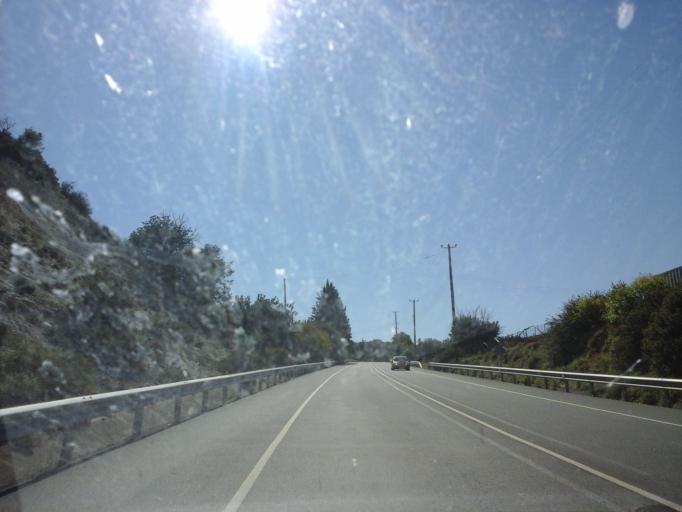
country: CY
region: Limassol
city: Pano Polemidia
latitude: 34.7680
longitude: 32.9446
